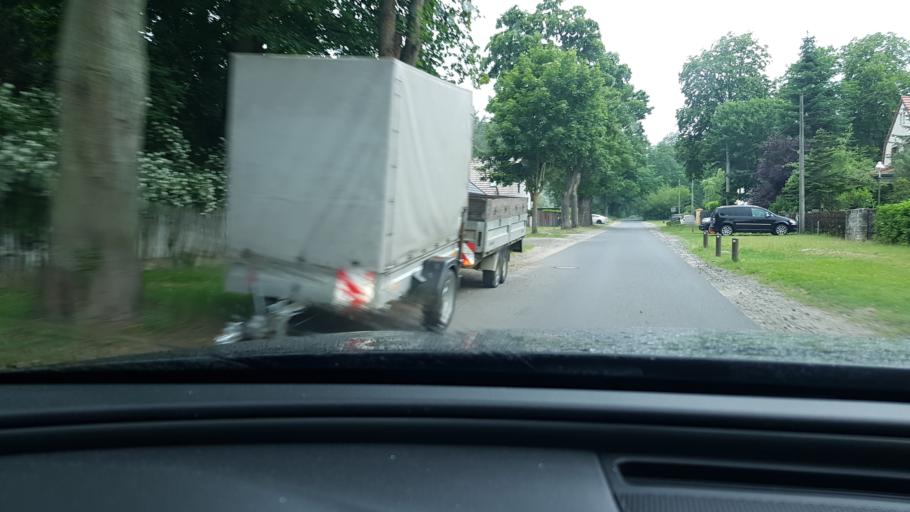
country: DE
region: Berlin
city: Lubars
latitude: 52.6288
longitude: 13.3615
